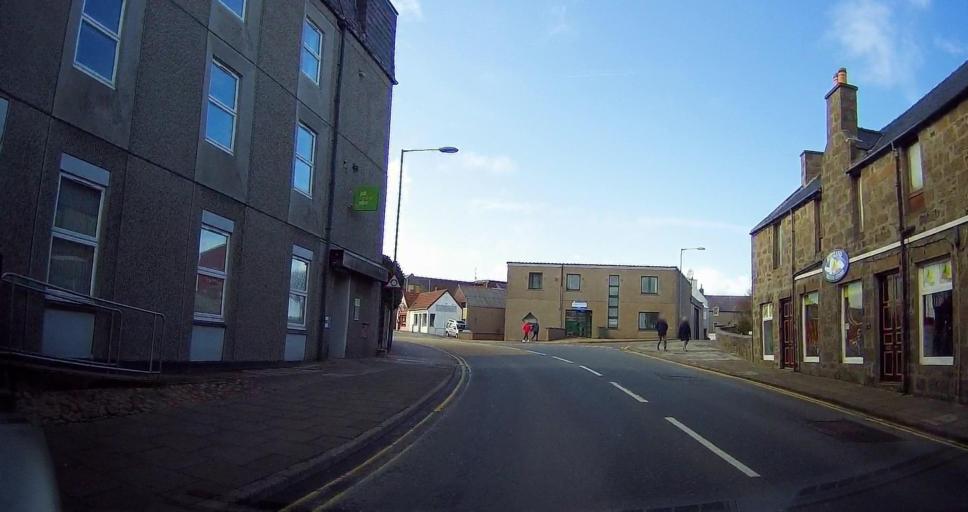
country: GB
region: Scotland
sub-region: Shetland Islands
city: Shetland
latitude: 60.1569
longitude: -1.1448
